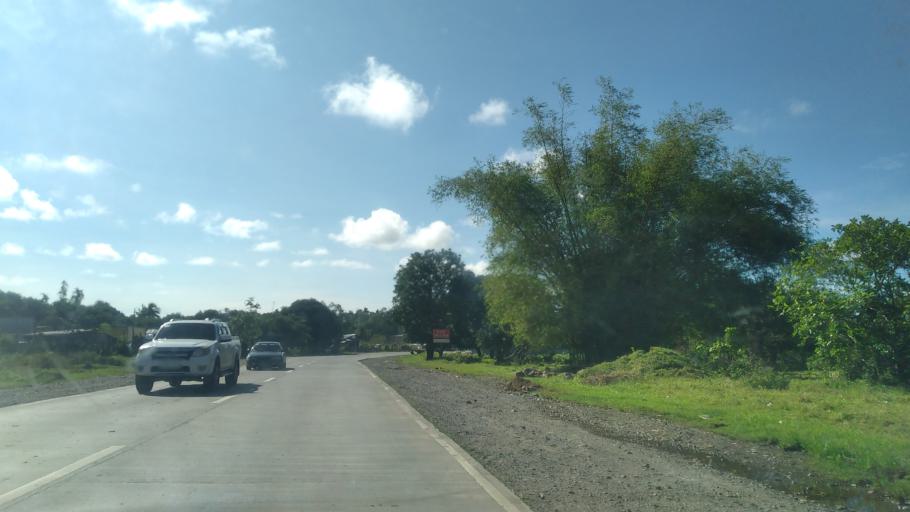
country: PH
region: Calabarzon
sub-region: Province of Quezon
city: Isabang
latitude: 13.9556
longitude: 121.5788
